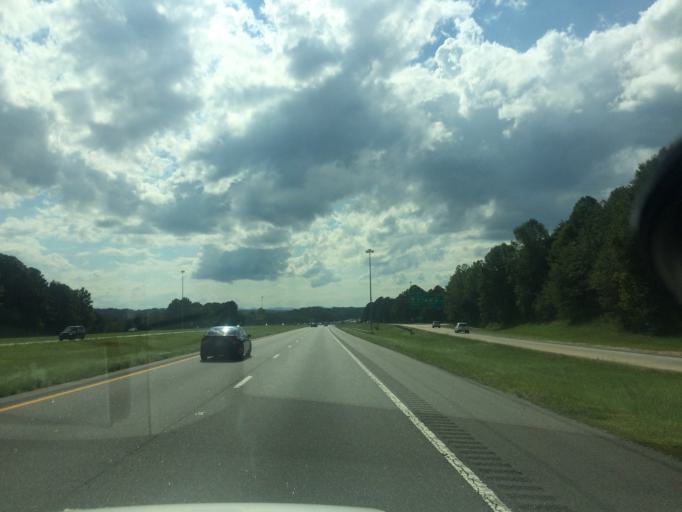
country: US
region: North Carolina
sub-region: Catawba County
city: Hickory
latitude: 35.7095
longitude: -81.3462
